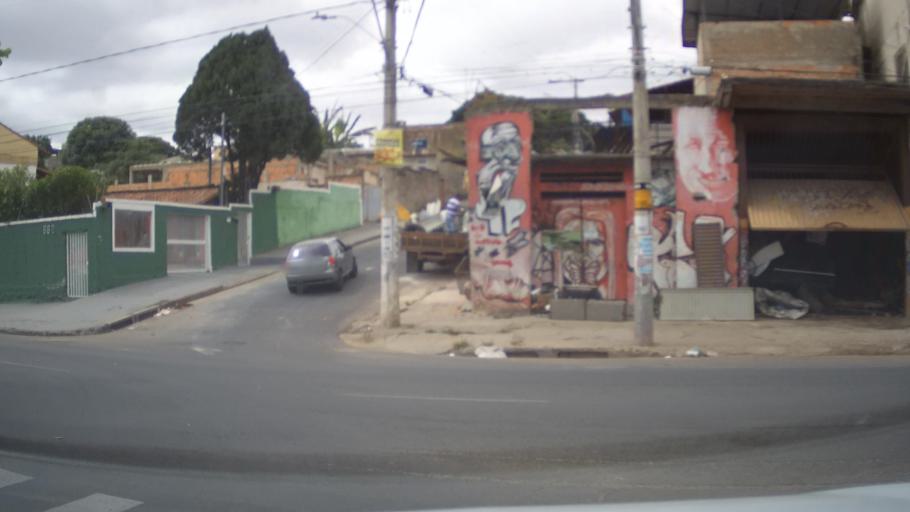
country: BR
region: Minas Gerais
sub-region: Belo Horizonte
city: Belo Horizonte
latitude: -19.8406
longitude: -43.9267
